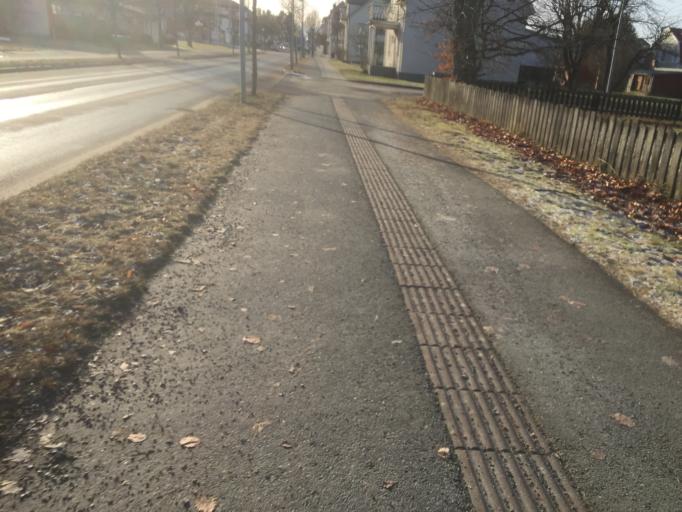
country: SE
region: Joenkoeping
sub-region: Aneby Kommun
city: Aneby
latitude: 57.8408
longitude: 14.8182
